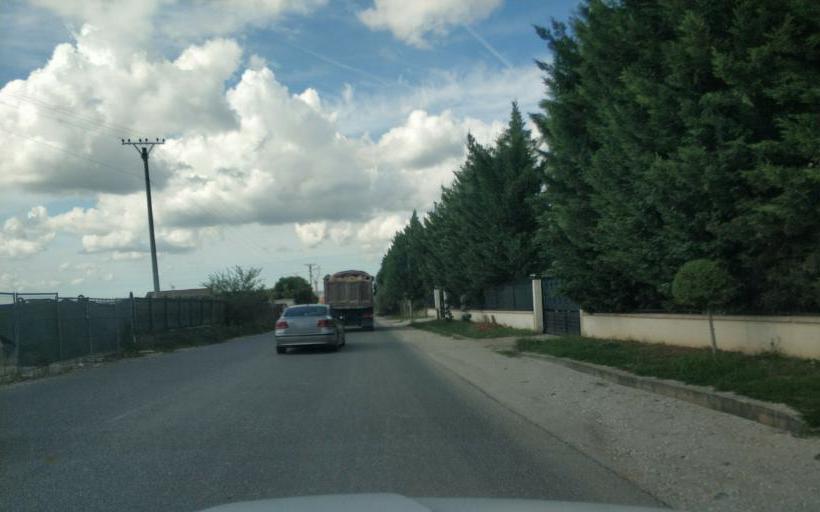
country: AL
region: Durres
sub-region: Rrethi i Krujes
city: Fushe-Kruje
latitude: 41.4761
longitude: 19.7482
